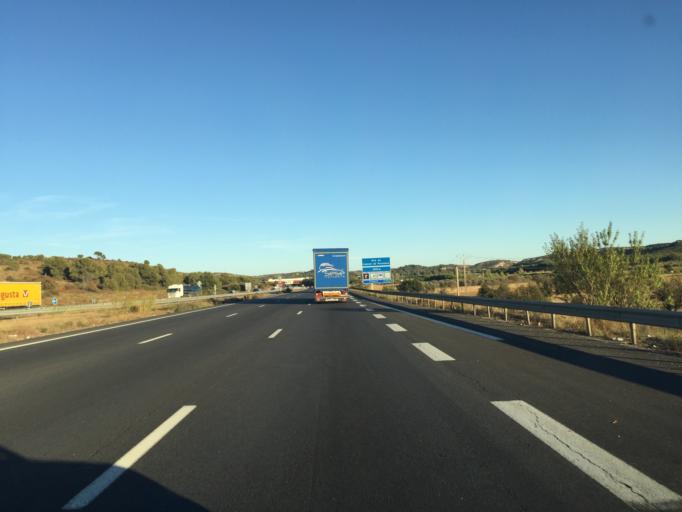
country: FR
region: Provence-Alpes-Cote d'Azur
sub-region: Departement des Bouches-du-Rhone
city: La Fare-les-Oliviers
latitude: 43.5923
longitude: 5.1781
